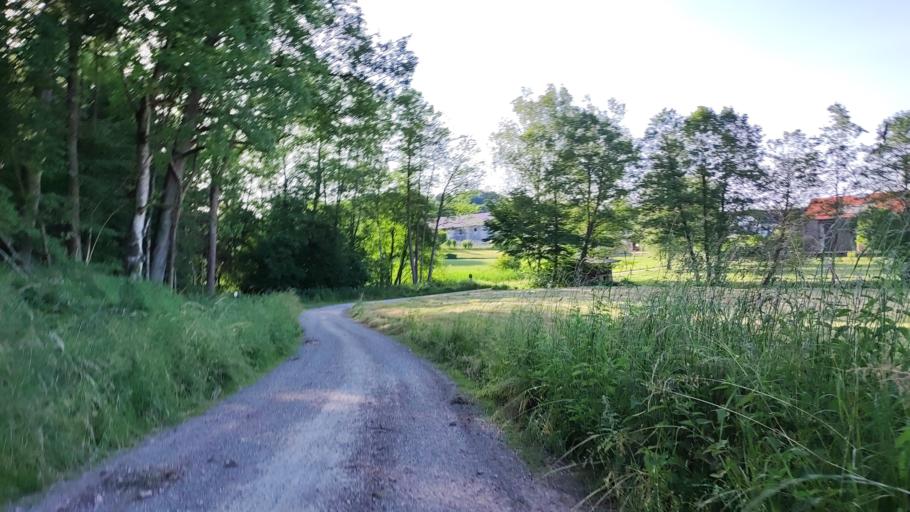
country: DE
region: Bavaria
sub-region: Swabia
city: Landensberg
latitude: 48.4300
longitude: 10.5058
